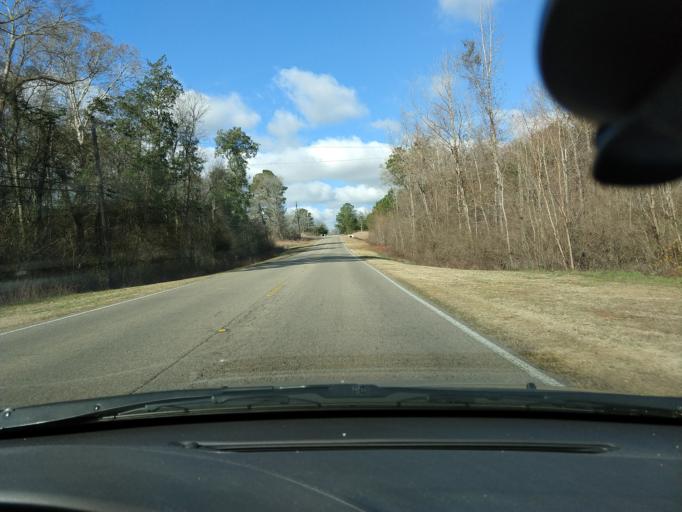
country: US
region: Alabama
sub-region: Coffee County
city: Enterprise
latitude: 31.3222
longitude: -85.8787
